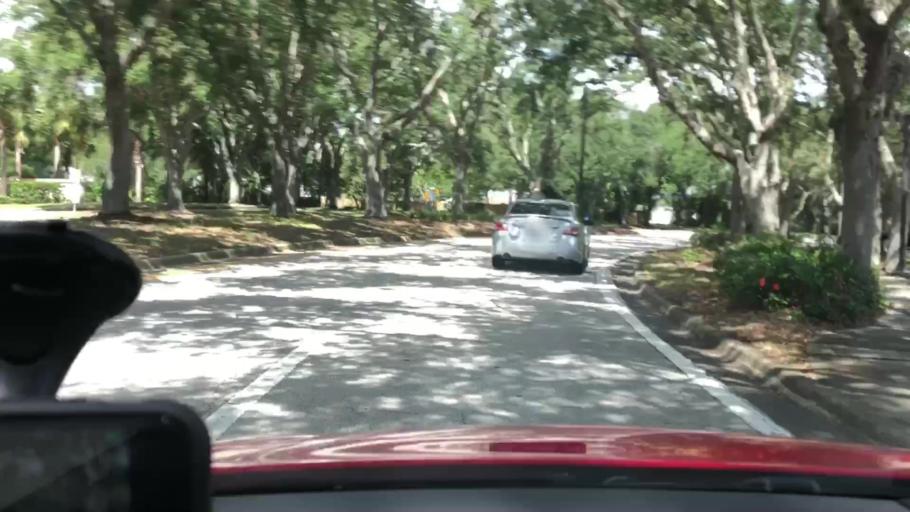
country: US
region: Florida
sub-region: Volusia County
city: Port Orange
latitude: 29.1207
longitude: -81.0181
